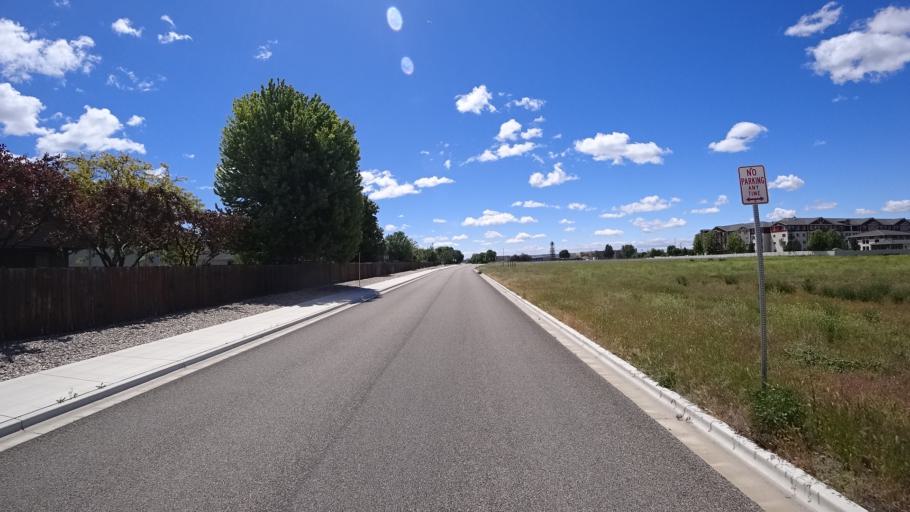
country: US
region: Idaho
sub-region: Ada County
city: Meridian
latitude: 43.6392
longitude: -116.3495
